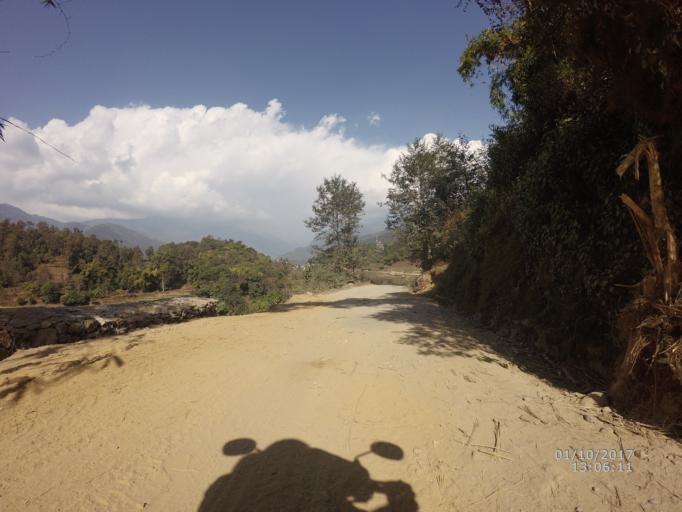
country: NP
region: Western Region
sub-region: Gandaki Zone
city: Pokhara
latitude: 28.3035
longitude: 83.9572
